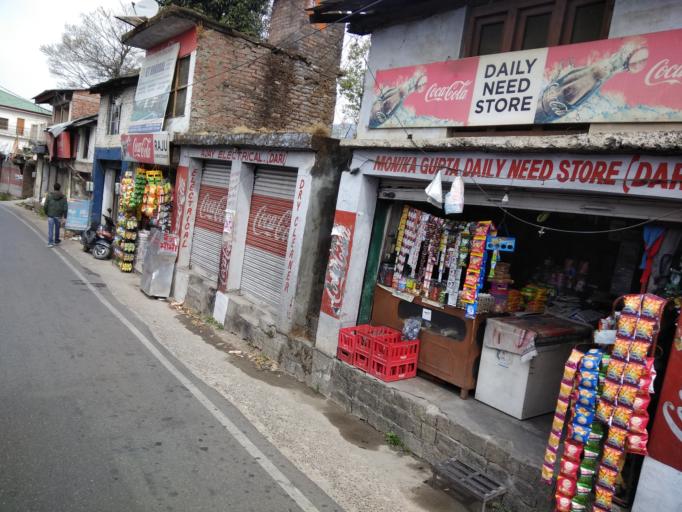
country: IN
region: Himachal Pradesh
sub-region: Kangra
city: Dharmsala
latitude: 32.1974
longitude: 76.3407
